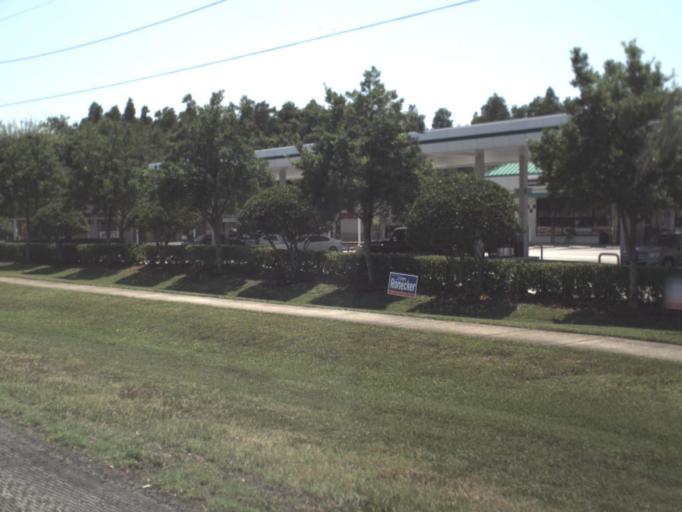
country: US
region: Florida
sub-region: Pinellas County
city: Saint George
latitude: 28.0778
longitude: -82.7393
